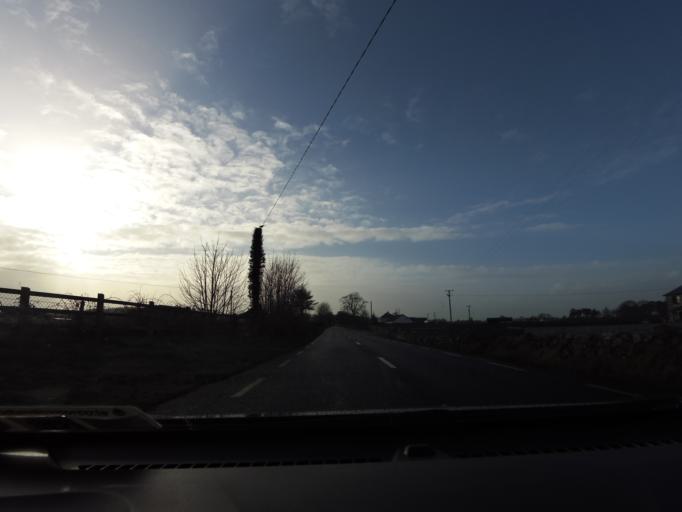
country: IE
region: Connaught
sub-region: County Galway
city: Tuam
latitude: 53.4916
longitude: -8.9768
